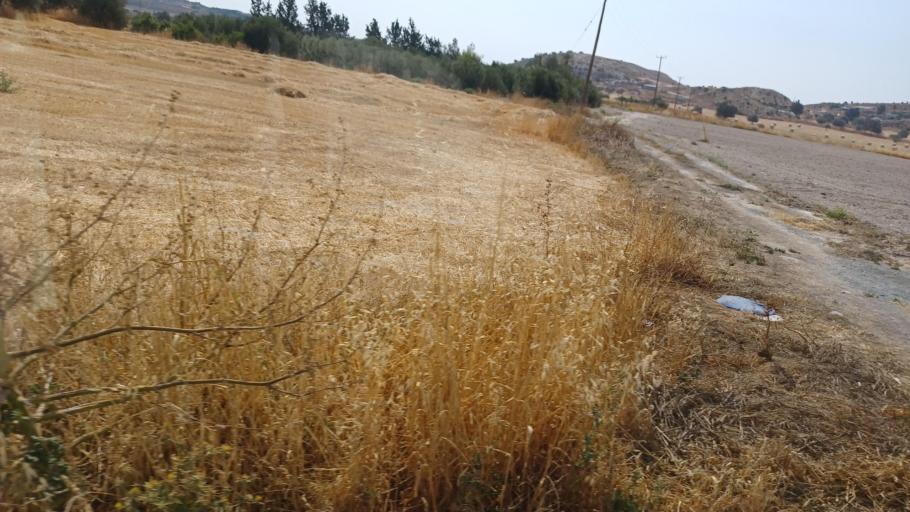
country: CY
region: Larnaka
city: Aradippou
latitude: 34.9231
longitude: 33.5376
